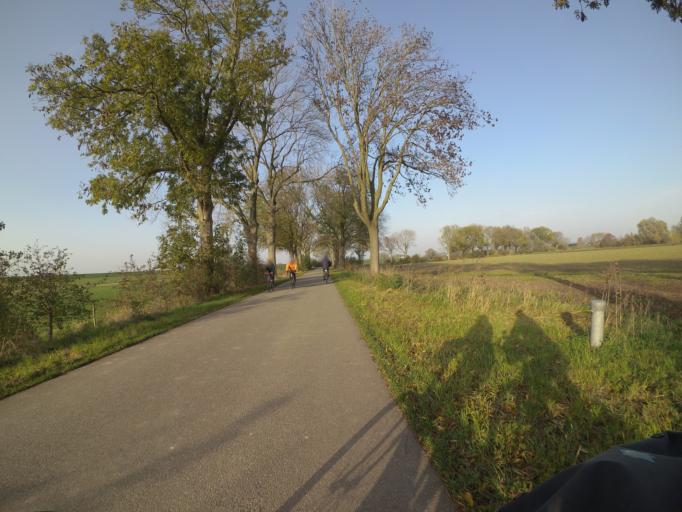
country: NL
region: Gelderland
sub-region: Gemeente Maasdriel
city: Heerewaarden
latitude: 51.8345
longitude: 5.4101
